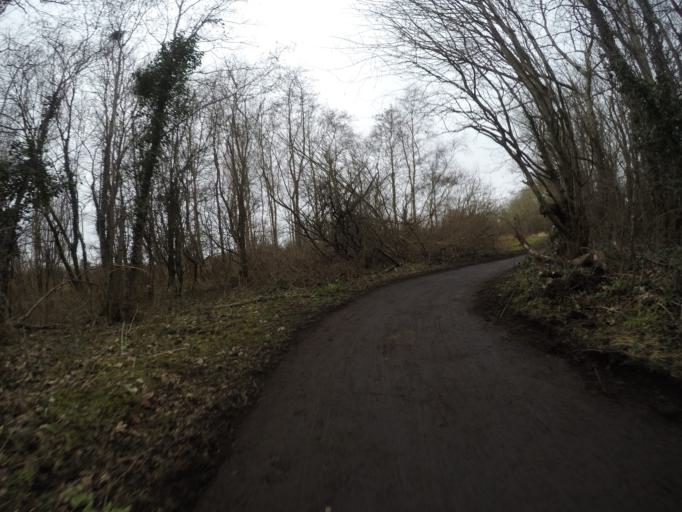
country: GB
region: Scotland
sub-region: North Ayrshire
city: Kilwinning
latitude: 55.6438
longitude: -4.6865
